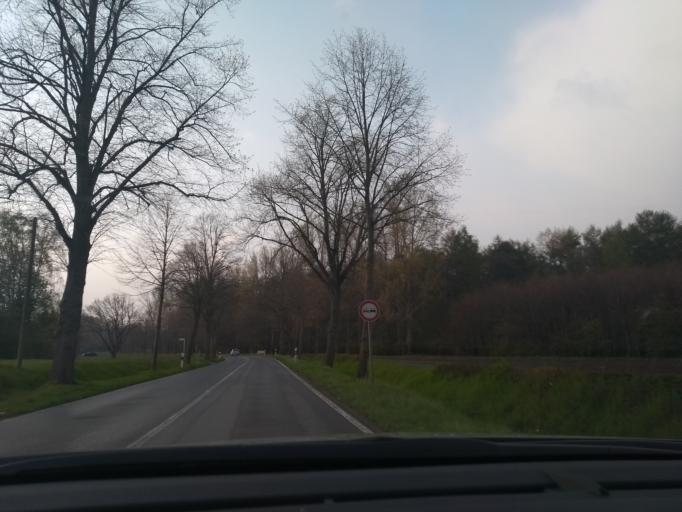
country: DE
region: North Rhine-Westphalia
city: Selm
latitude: 51.6398
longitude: 7.4712
